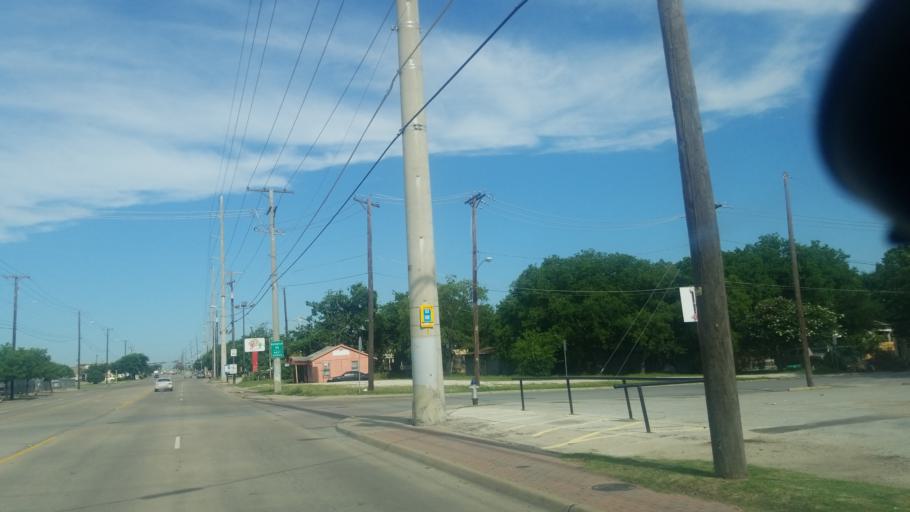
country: US
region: Texas
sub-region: Dallas County
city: Dallas
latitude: 32.7787
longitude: -96.8531
